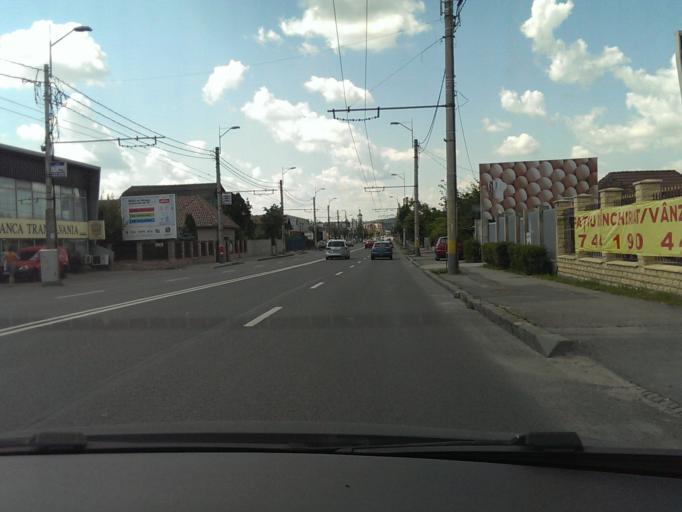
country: RO
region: Cluj
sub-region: Comuna Apahida
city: Sannicoara
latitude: 46.7805
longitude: 23.6662
